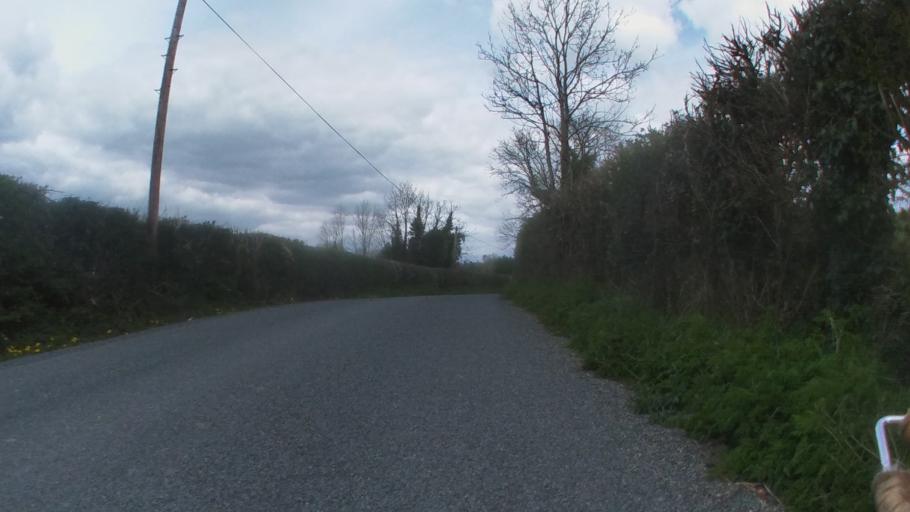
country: IE
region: Leinster
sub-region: Kilkenny
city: Kilkenny
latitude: 52.6539
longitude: -7.1833
